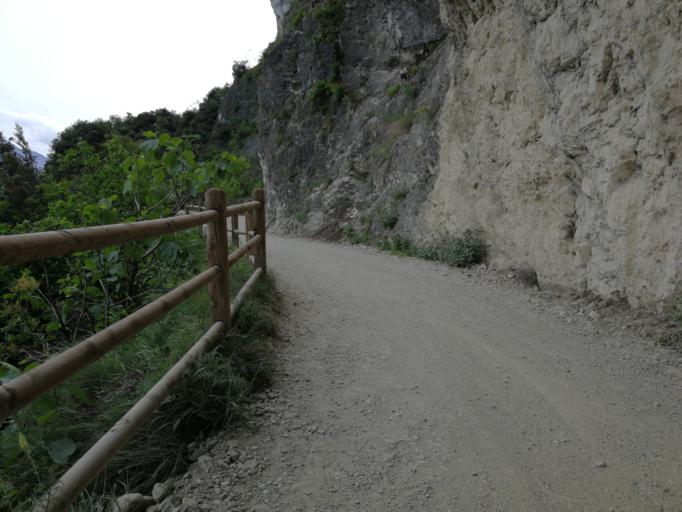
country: IT
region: Trentino-Alto Adige
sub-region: Provincia di Trento
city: Riva del Garda
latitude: 45.8756
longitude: 10.8381
